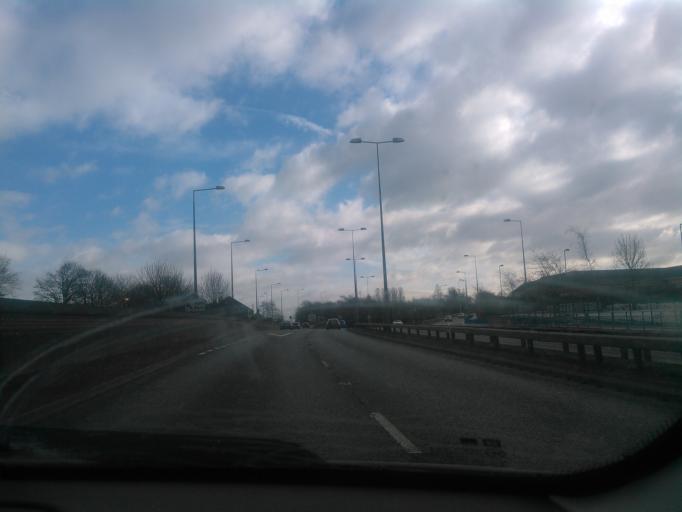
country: GB
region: England
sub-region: Staffordshire
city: Longton
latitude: 52.9744
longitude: -2.0908
